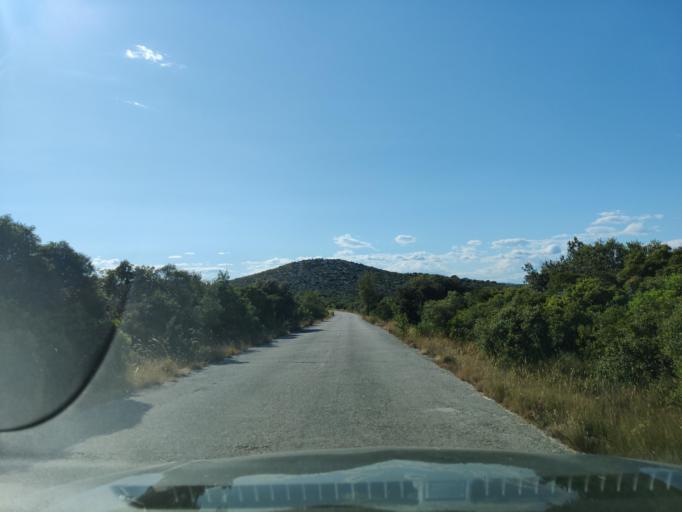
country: HR
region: Sibensko-Kniniska
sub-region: Grad Sibenik
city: Sibenik
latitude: 43.7380
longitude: 15.8726
